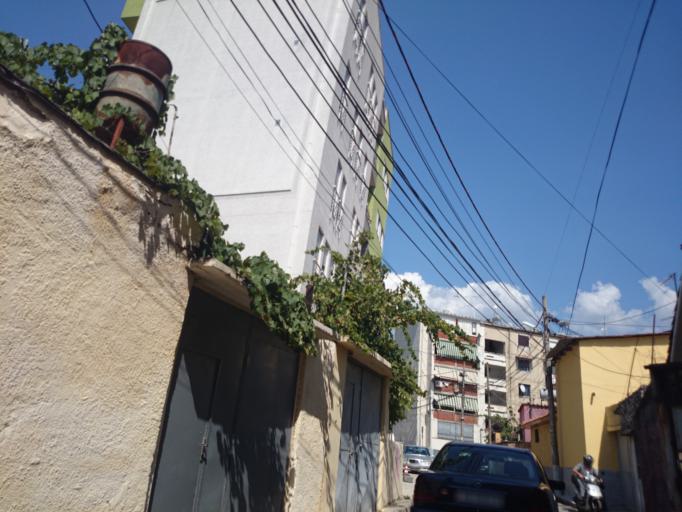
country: AL
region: Tirane
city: Tirana
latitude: 41.3280
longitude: 19.8325
